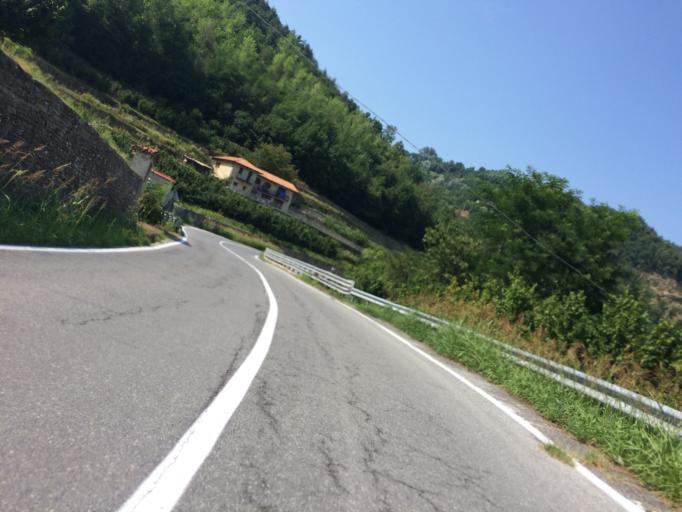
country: IT
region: Piedmont
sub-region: Provincia di Cuneo
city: Torre Bormida
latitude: 44.5786
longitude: 8.1658
